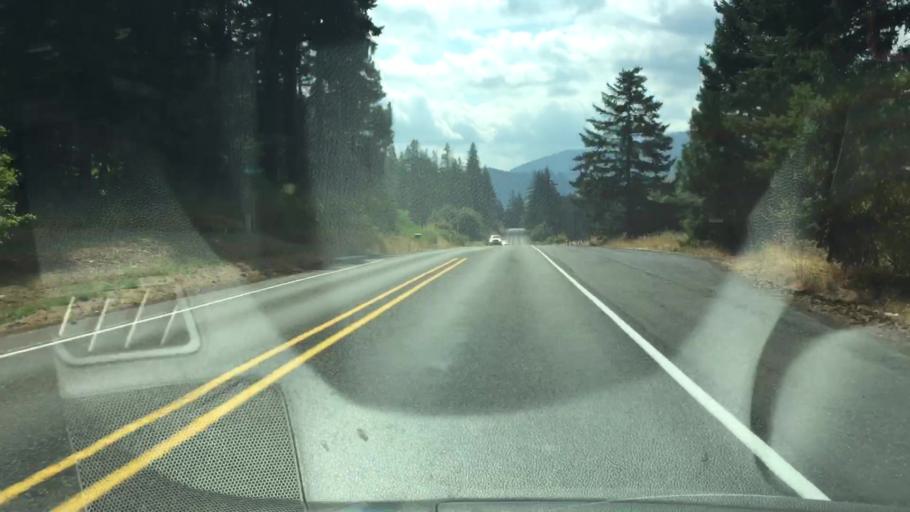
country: US
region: Washington
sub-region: Klickitat County
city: White Salmon
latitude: 45.7868
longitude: -121.4995
